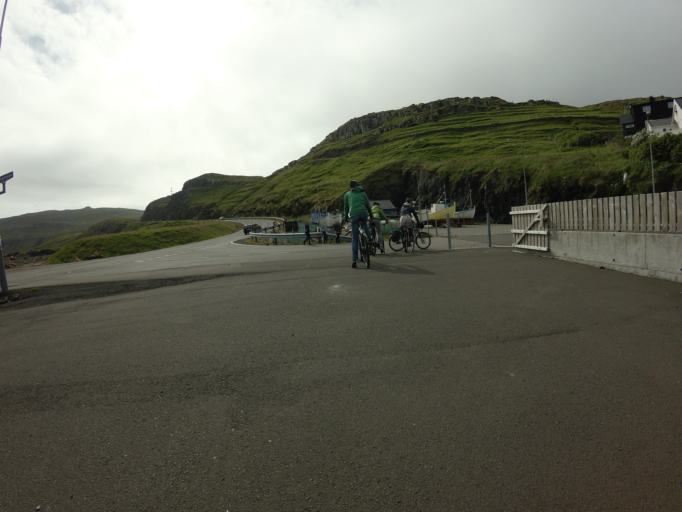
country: FO
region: Sandoy
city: Sandur
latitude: 61.9022
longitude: -6.8784
